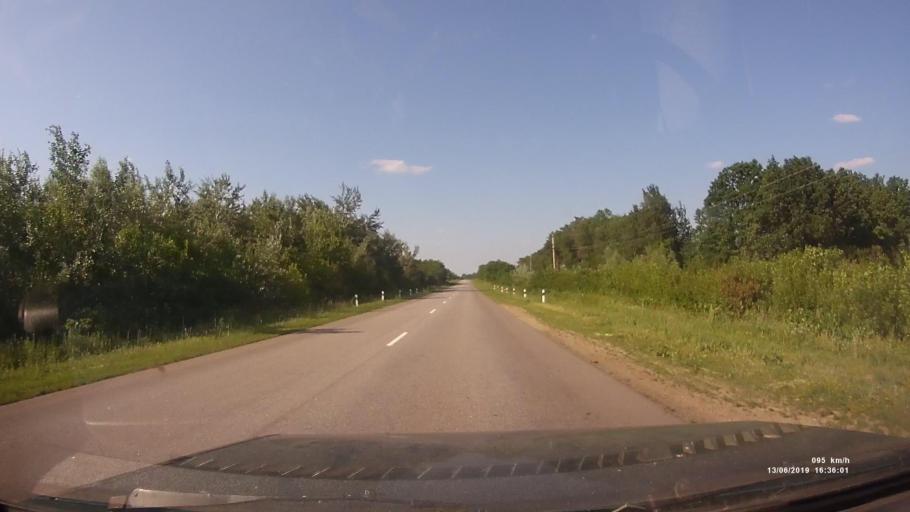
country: RU
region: Rostov
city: Kazanskaya
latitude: 49.8896
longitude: 41.3028
